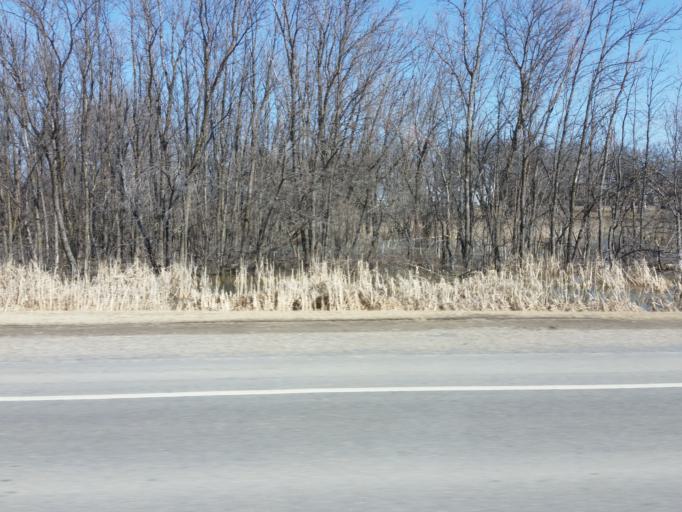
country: US
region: North Dakota
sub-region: Walsh County
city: Grafton
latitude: 48.2830
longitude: -97.3694
